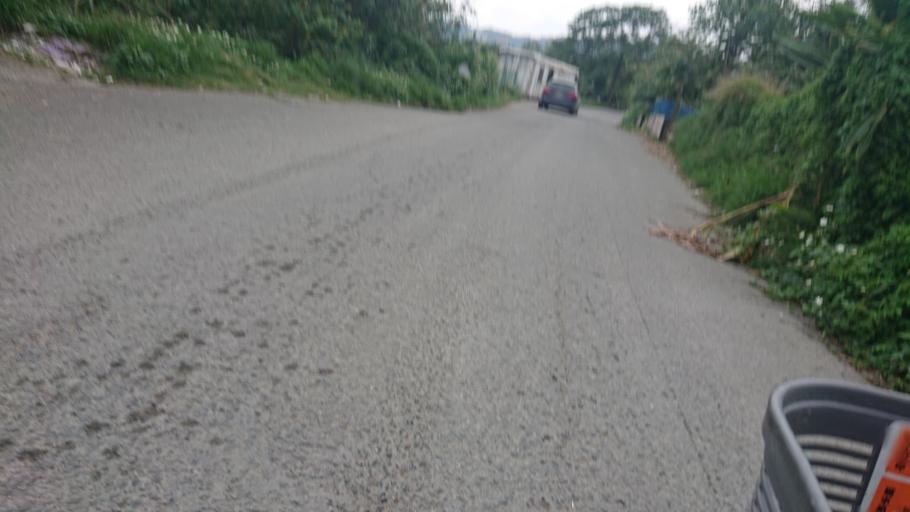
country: TW
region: Taiwan
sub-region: Taoyuan
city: Taoyuan
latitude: 24.9434
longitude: 121.3580
